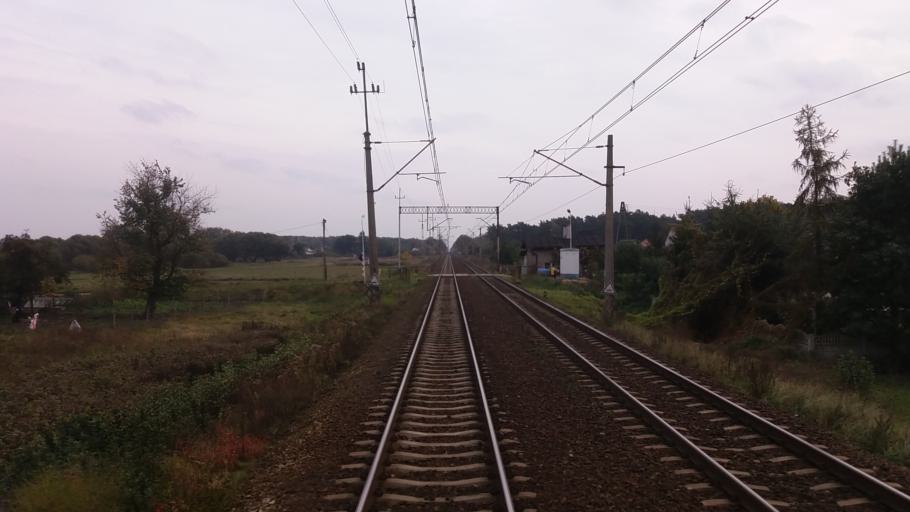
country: PL
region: West Pomeranian Voivodeship
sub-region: Powiat gryfinski
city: Stare Czarnowo
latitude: 53.3850
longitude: 14.7468
